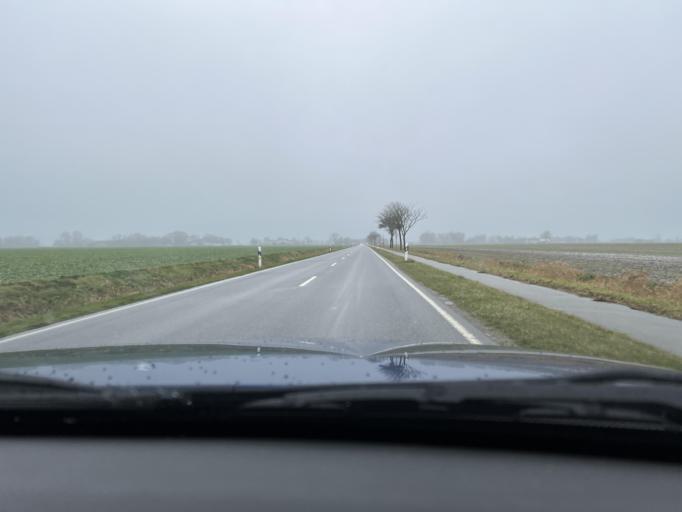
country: DE
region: Schleswig-Holstein
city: Stelle-Wittenwurth
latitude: 54.2408
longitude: 9.0213
